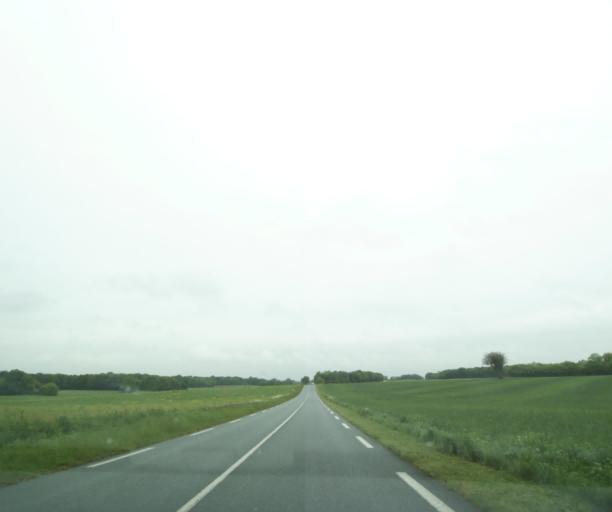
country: FR
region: Poitou-Charentes
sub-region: Departement de la Charente-Maritime
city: Nieul-les-Saintes
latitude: 45.7449
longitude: -0.7179
